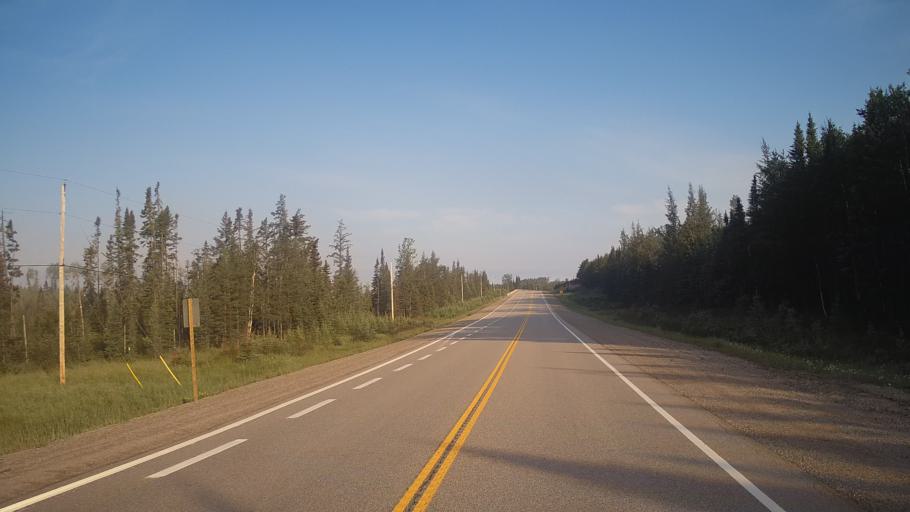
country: CA
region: Ontario
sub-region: Rainy River District
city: Atikokan
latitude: 49.3372
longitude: -91.4660
